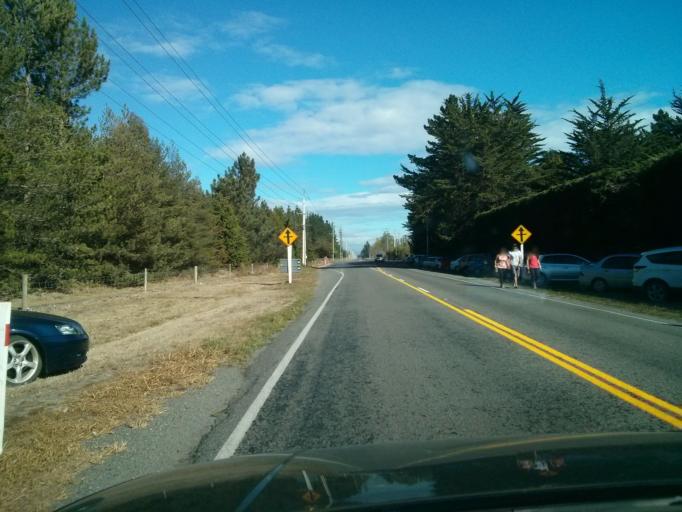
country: NZ
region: Canterbury
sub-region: Waimakariri District
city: Kaiapoi
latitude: -43.3678
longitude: 172.4912
